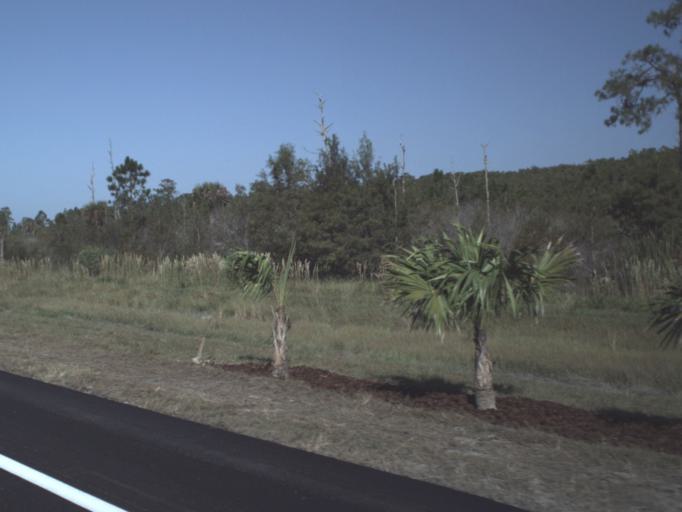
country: US
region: Florida
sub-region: Lee County
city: Three Oaks
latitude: 26.5121
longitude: -81.7776
